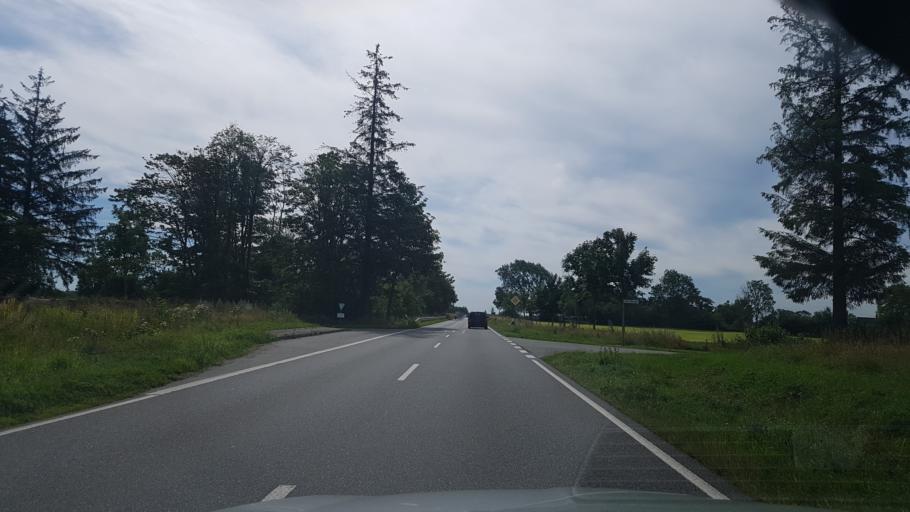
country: DE
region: Schleswig-Holstein
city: Osterby
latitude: 54.8188
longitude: 9.2243
